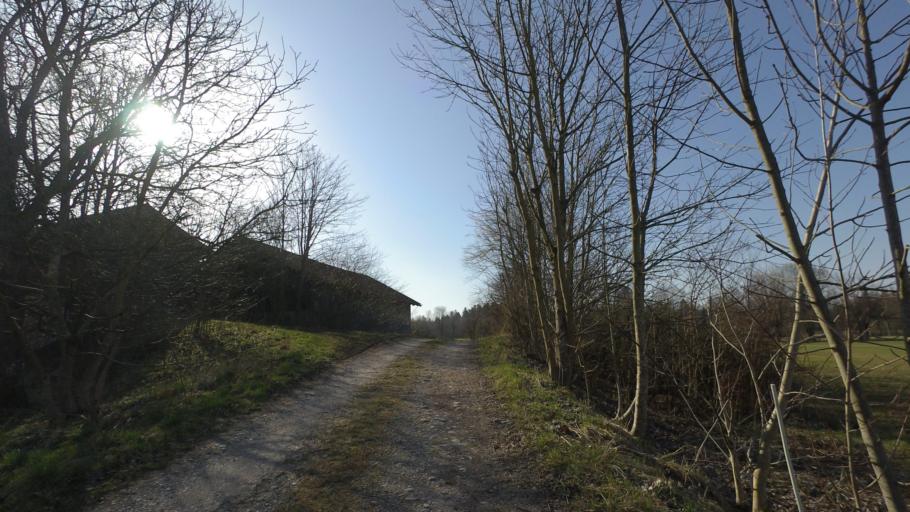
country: DE
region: Bavaria
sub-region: Upper Bavaria
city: Chieming
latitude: 47.9353
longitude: 12.5497
